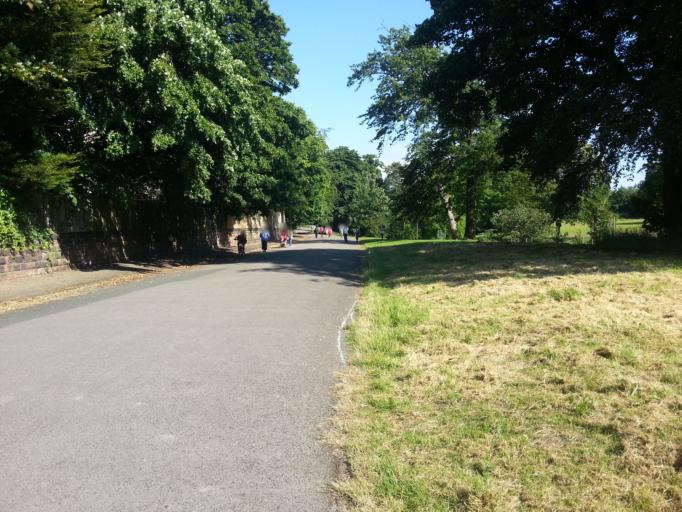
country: GB
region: England
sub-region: Liverpool
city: Liverpool
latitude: 53.3894
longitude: -2.9539
